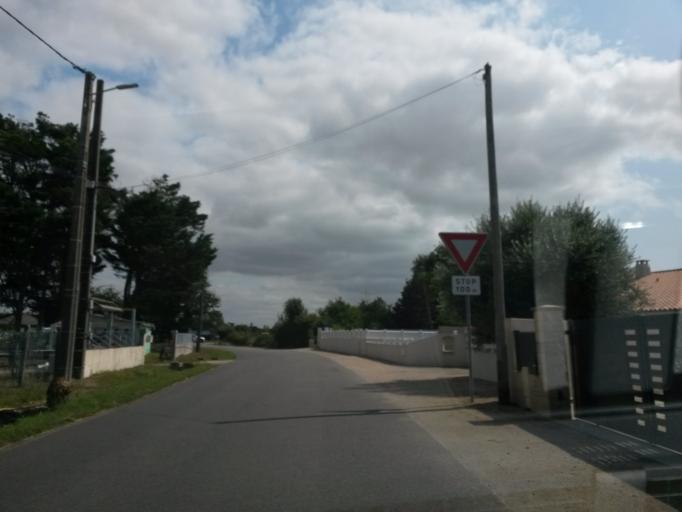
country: FR
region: Pays de la Loire
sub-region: Departement de la Vendee
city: Jard-sur-Mer
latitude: 46.4340
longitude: -1.5795
